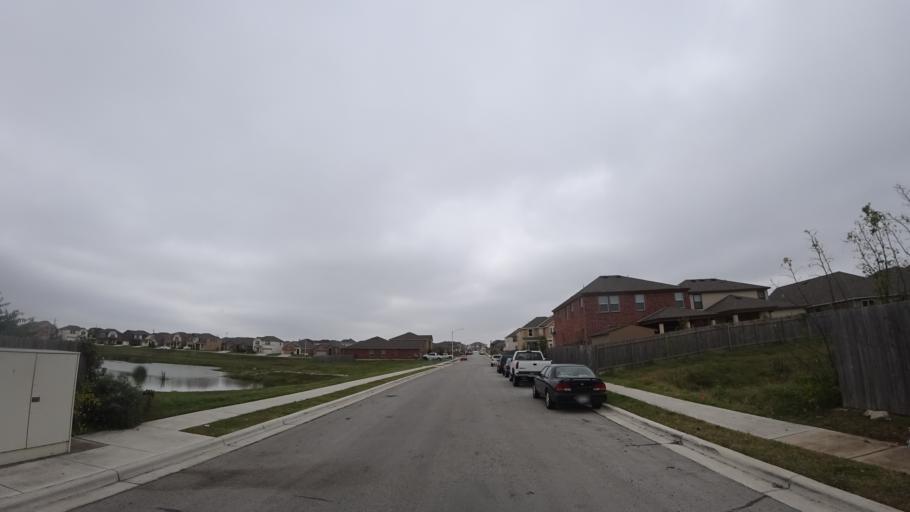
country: US
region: Texas
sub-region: Travis County
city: Pflugerville
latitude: 30.3951
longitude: -97.6471
